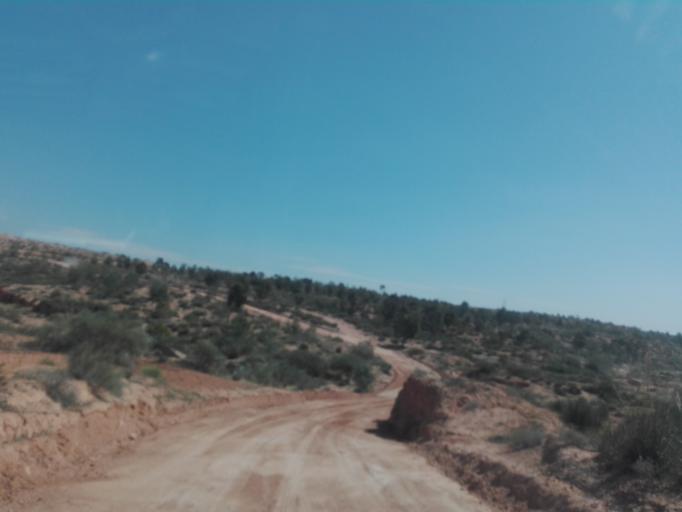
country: TN
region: Safaqis
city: Sfax
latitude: 34.6943
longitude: 10.5311
